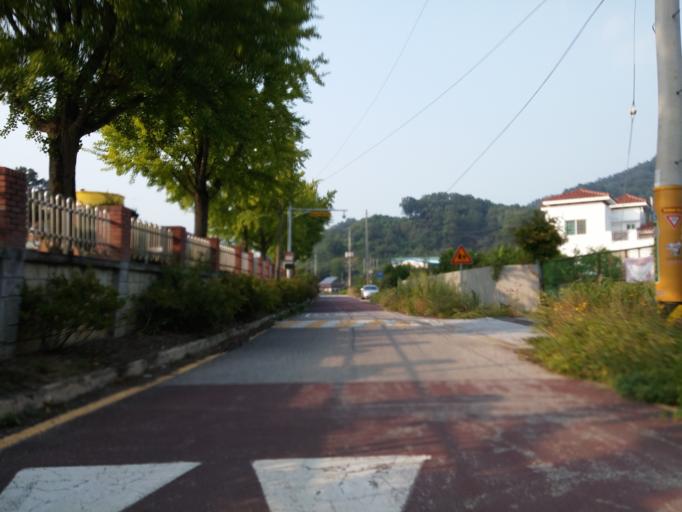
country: KR
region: Chungcheongbuk-do
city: Okcheon
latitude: 36.3333
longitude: 127.5240
